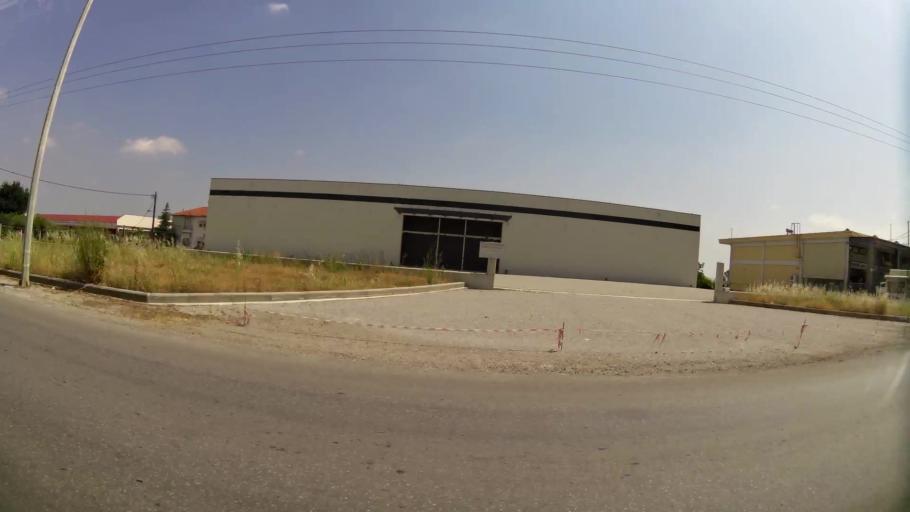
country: GR
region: Central Macedonia
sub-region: Nomos Imathias
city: Veroia
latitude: 40.5127
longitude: 22.2146
